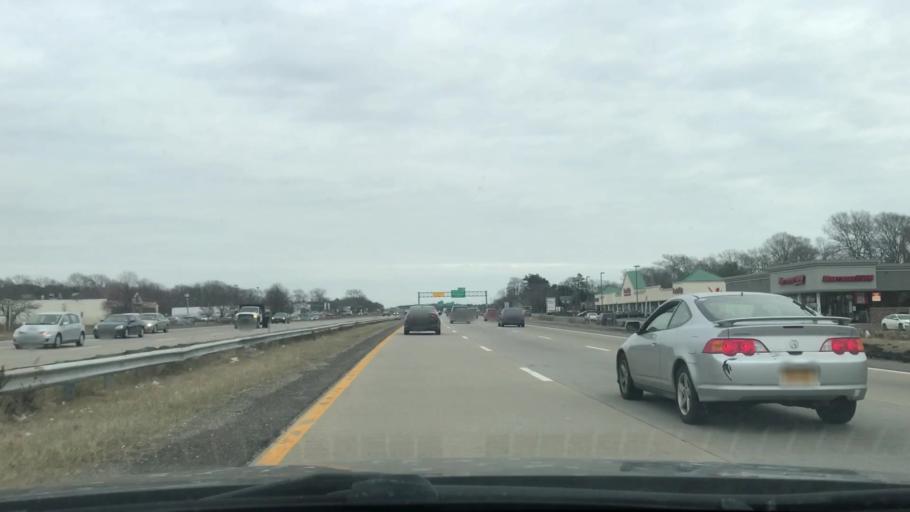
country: US
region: New York
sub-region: Suffolk County
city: North Patchogue
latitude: 40.7800
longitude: -73.0044
